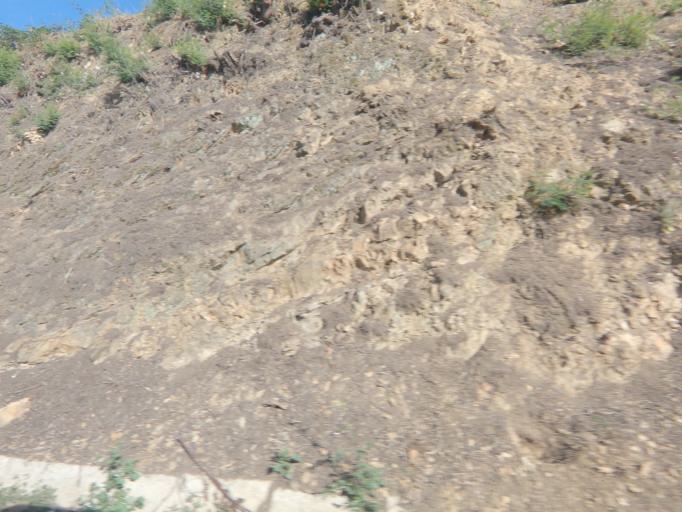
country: PT
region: Vila Real
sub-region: Sabrosa
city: Sabrosa
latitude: 41.2471
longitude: -7.5789
